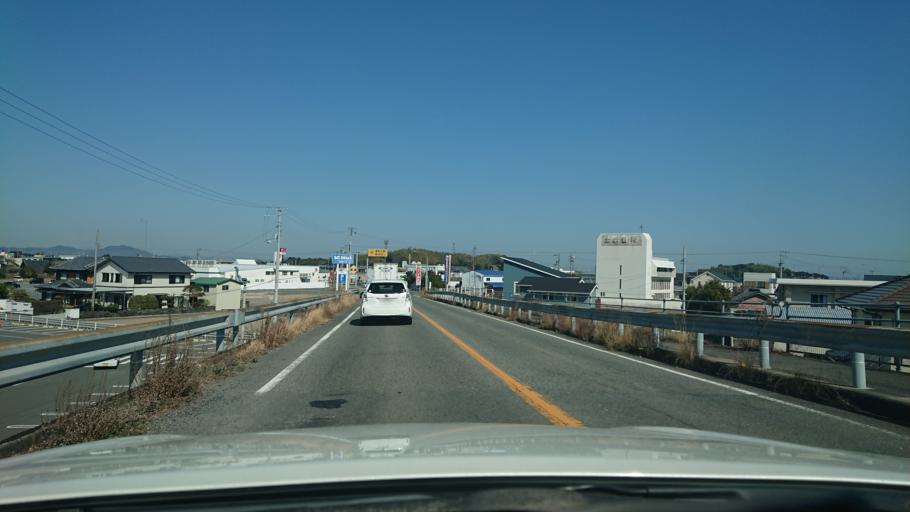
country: JP
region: Tokushima
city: Anan
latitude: 33.9593
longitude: 134.6234
